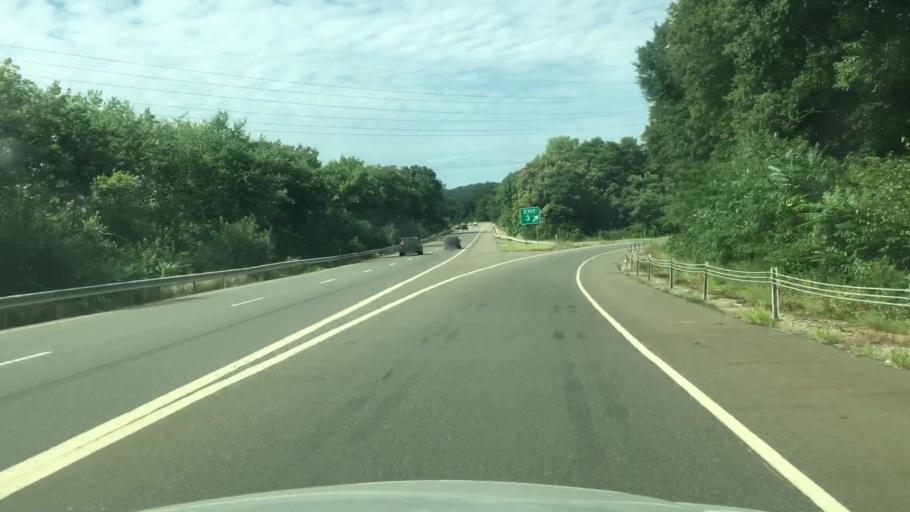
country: US
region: Connecticut
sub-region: Middlesex County
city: Essex Village
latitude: 41.3478
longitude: -72.4011
